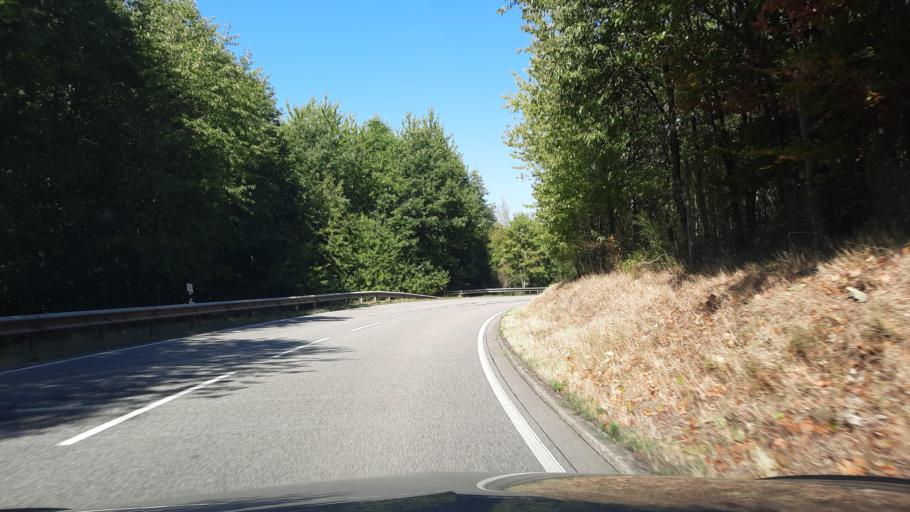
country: DE
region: Rheinland-Pfalz
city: Irsch
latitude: 49.5941
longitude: 6.5944
